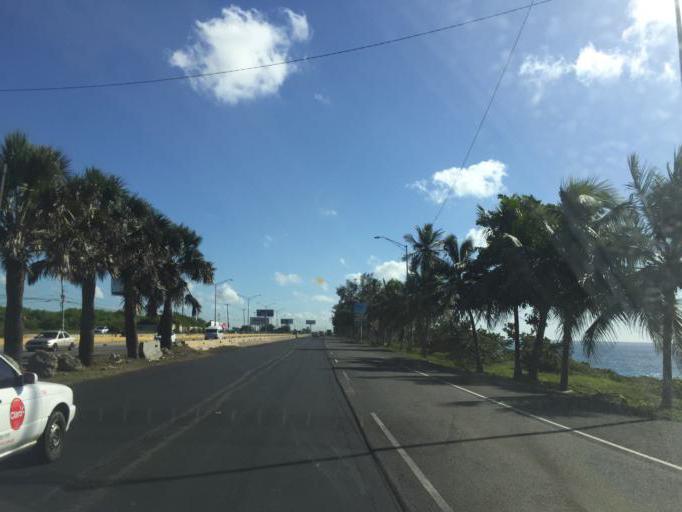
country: DO
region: Santo Domingo
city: Guerra
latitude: 18.4636
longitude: -69.7514
